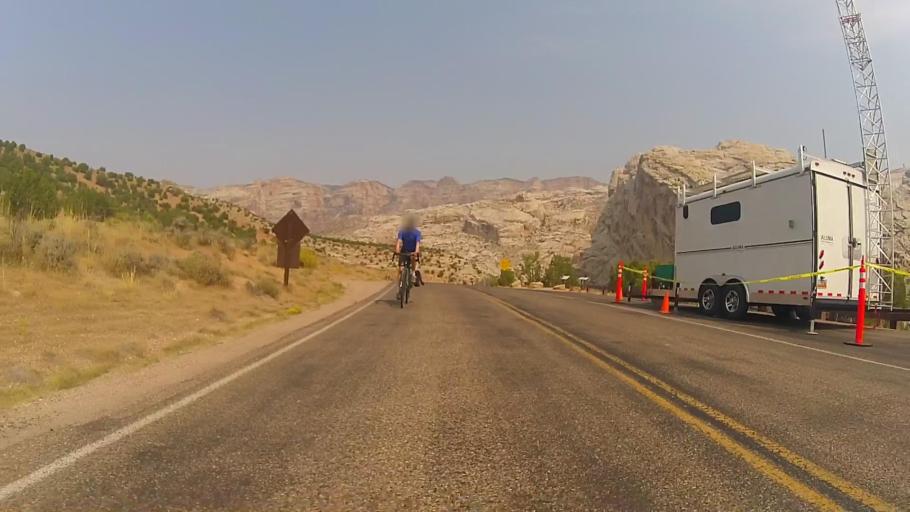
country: US
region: Utah
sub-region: Uintah County
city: Naples
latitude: 40.4425
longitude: -109.2541
